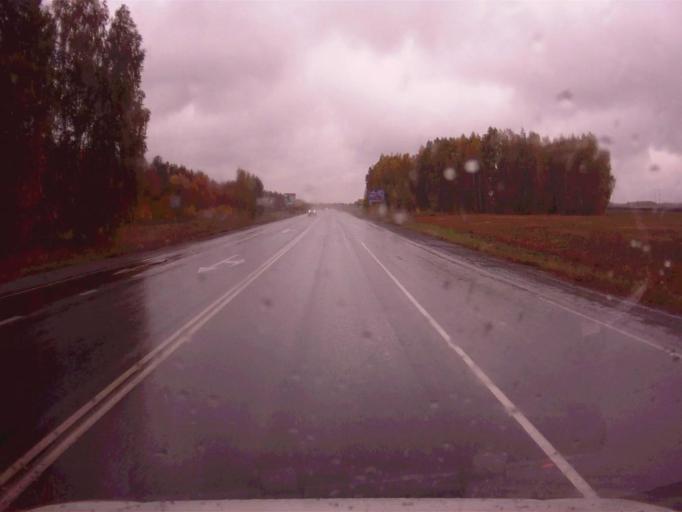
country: RU
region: Chelyabinsk
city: Roshchino
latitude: 55.3957
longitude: 61.0966
